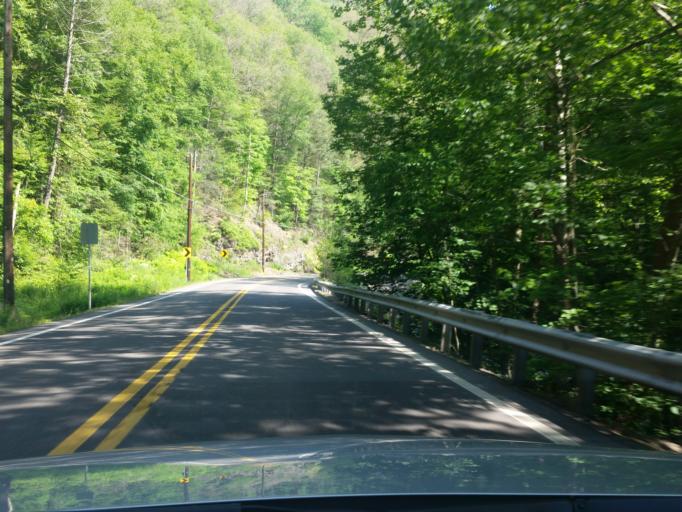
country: US
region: Pennsylvania
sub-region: Luzerne County
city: Nanticoke
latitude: 41.2273
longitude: -76.0125
